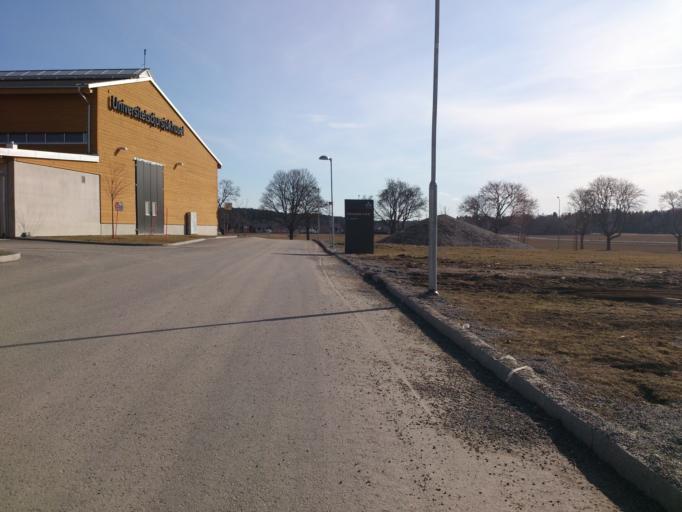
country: SE
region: Uppsala
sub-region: Uppsala Kommun
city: Saevja
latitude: 59.8149
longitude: 17.6542
